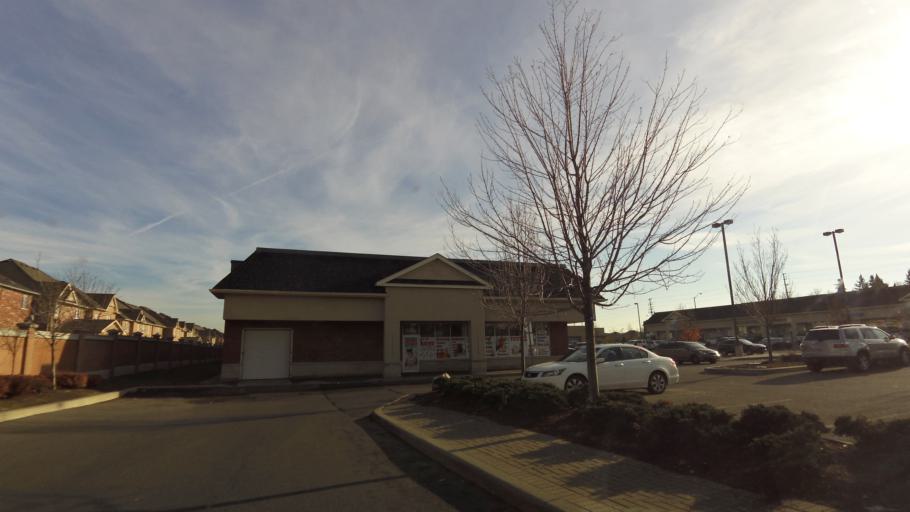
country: CA
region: Ontario
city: Brampton
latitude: 43.7716
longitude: -79.7552
